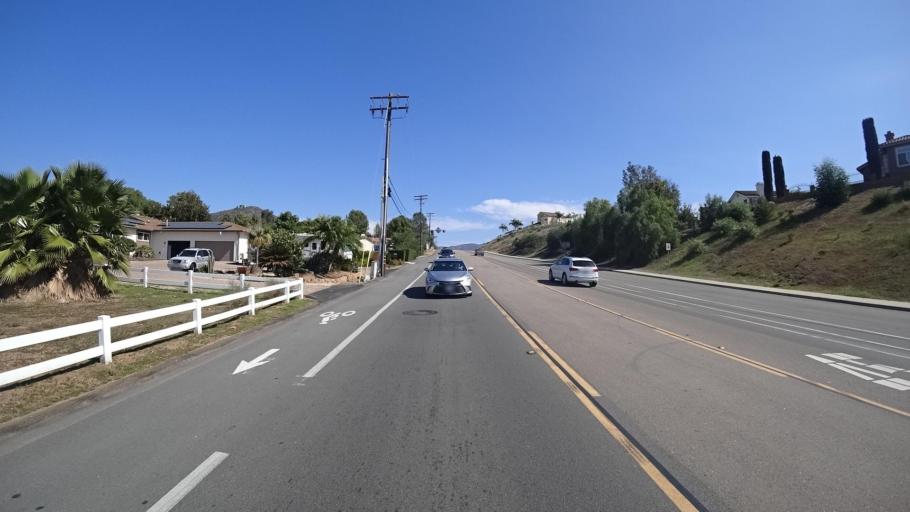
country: US
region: California
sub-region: San Diego County
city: Rancho San Diego
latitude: 32.7622
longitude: -116.9146
